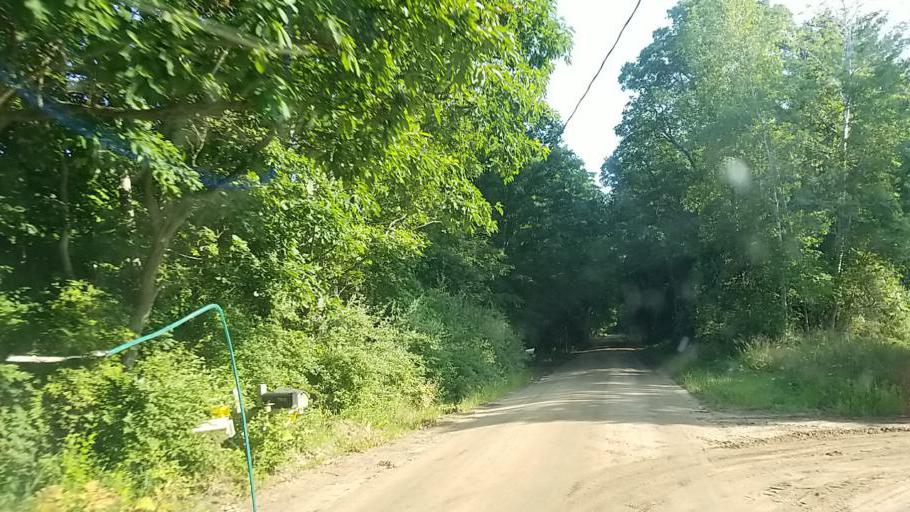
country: US
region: Michigan
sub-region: Newaygo County
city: Newaygo
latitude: 43.3736
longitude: -85.8503
